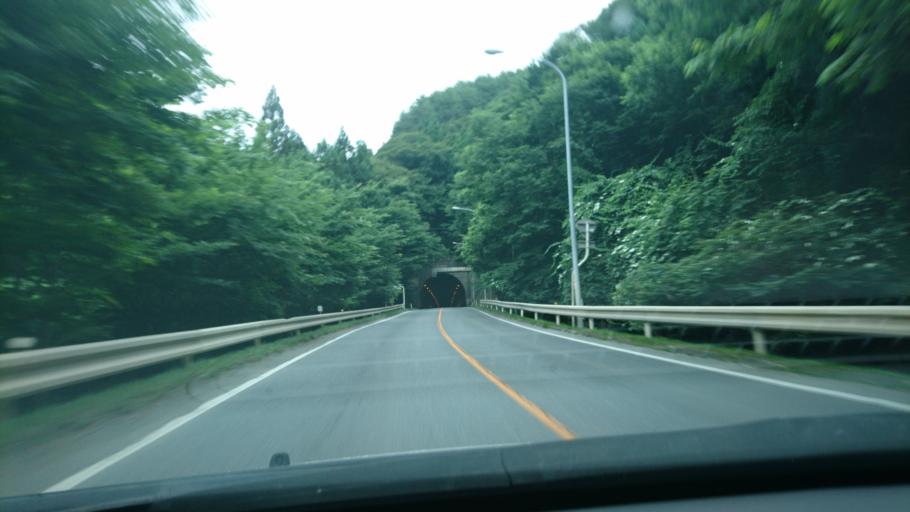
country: JP
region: Iwate
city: Kamaishi
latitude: 39.2205
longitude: 141.8743
